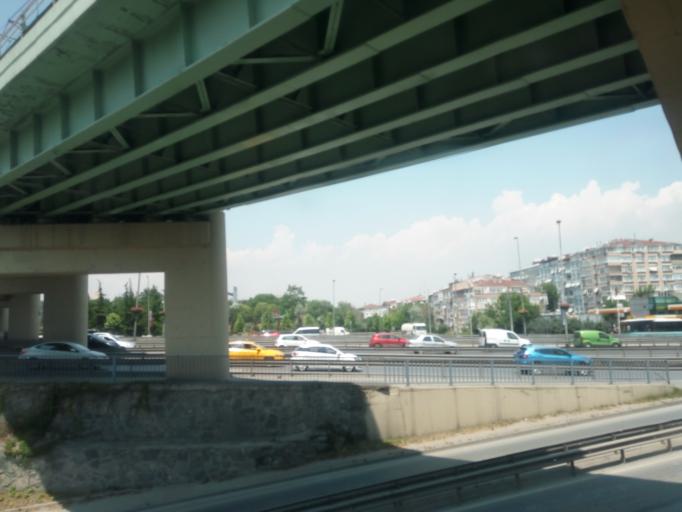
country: TR
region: Istanbul
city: guengoeren merter
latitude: 41.0012
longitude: 28.8858
